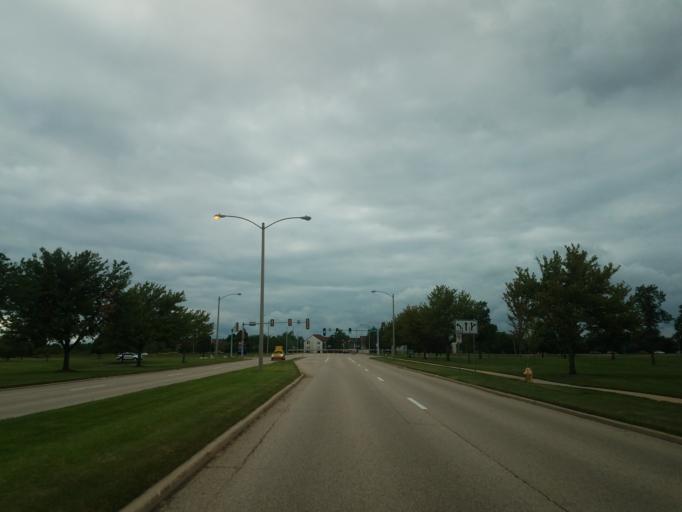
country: US
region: Illinois
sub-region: McLean County
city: Bloomington
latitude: 40.4618
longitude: -88.9557
